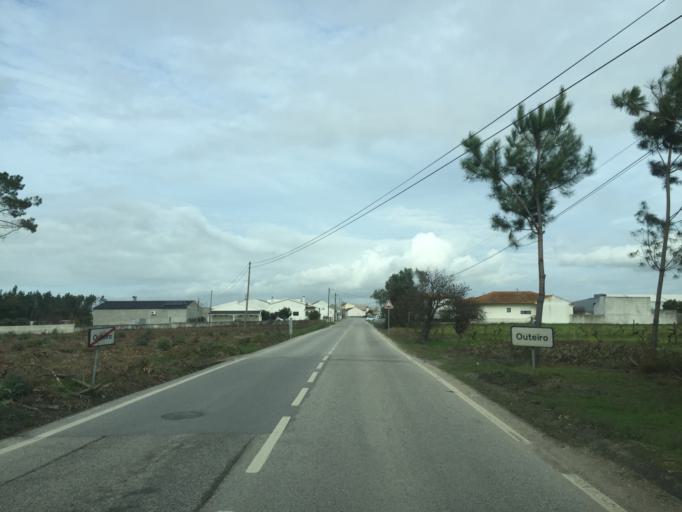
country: PT
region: Coimbra
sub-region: Figueira da Foz
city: Lavos
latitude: 40.0530
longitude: -8.8153
